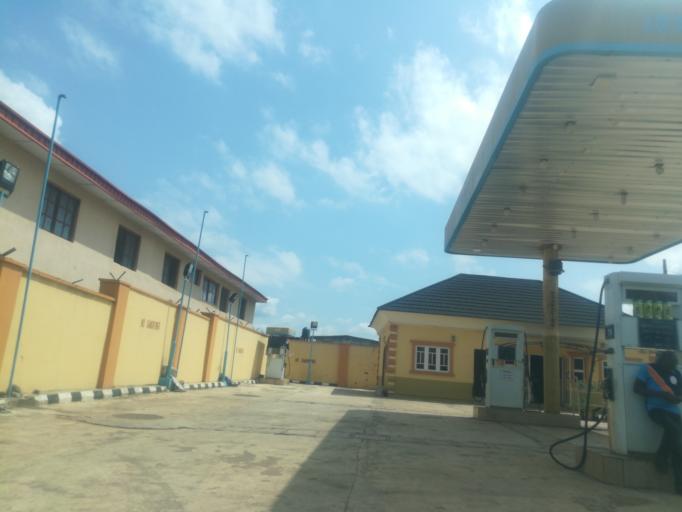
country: NG
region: Oyo
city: Egbeda
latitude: 7.4250
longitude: 3.9950
